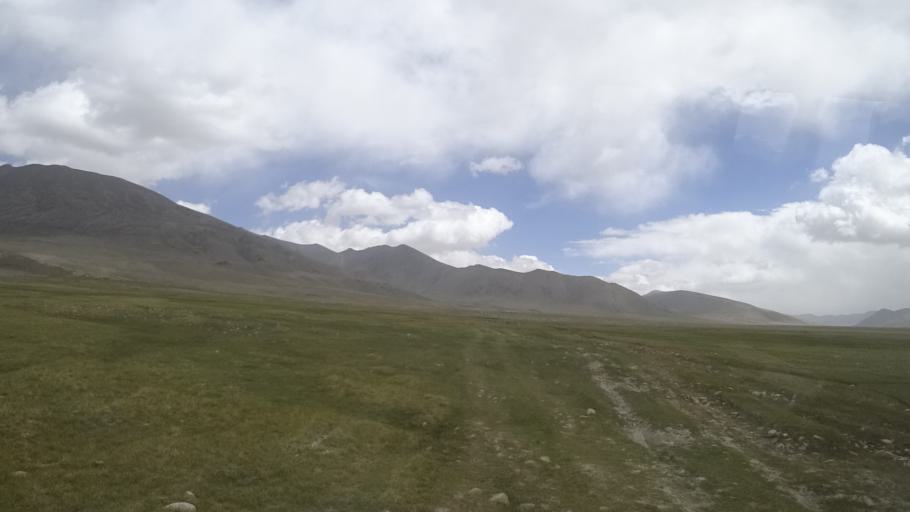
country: TJ
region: Gorno-Badakhshan
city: Murghob
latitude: 37.4865
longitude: 73.9897
